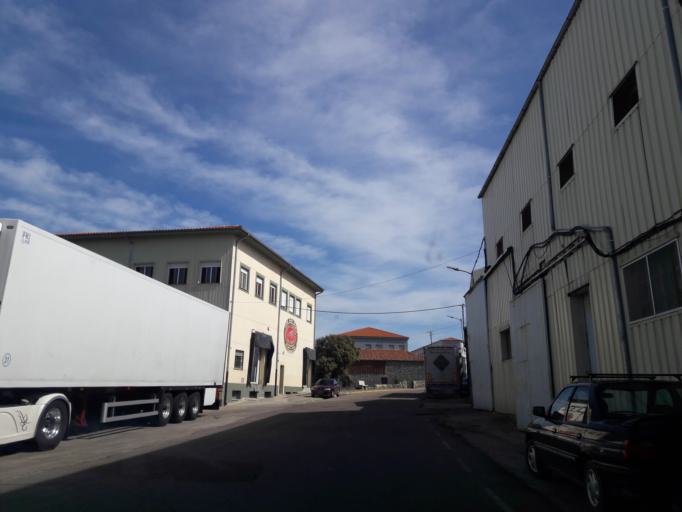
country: ES
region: Castille and Leon
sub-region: Provincia de Salamanca
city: Ledrada
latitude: 40.4653
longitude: -5.7220
